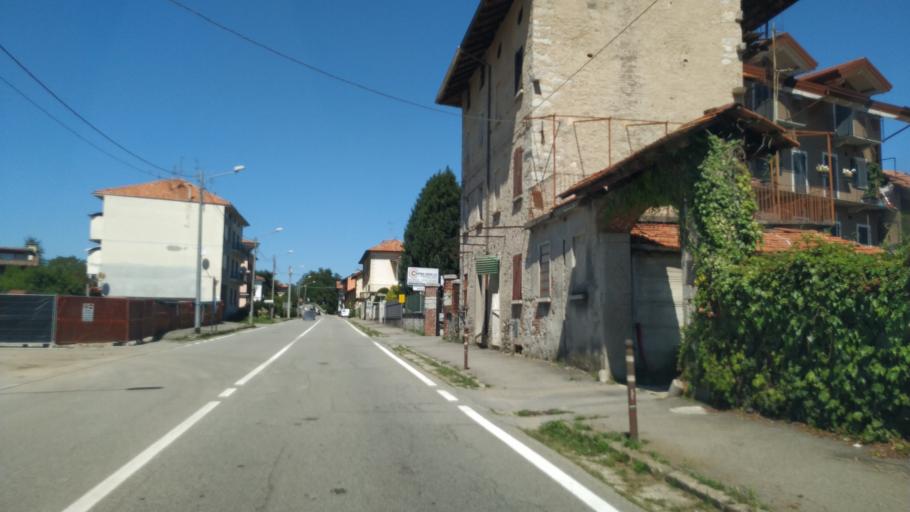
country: IT
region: Piedmont
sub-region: Provincia di Novara
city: Borgomanero
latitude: 45.7043
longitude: 8.4682
